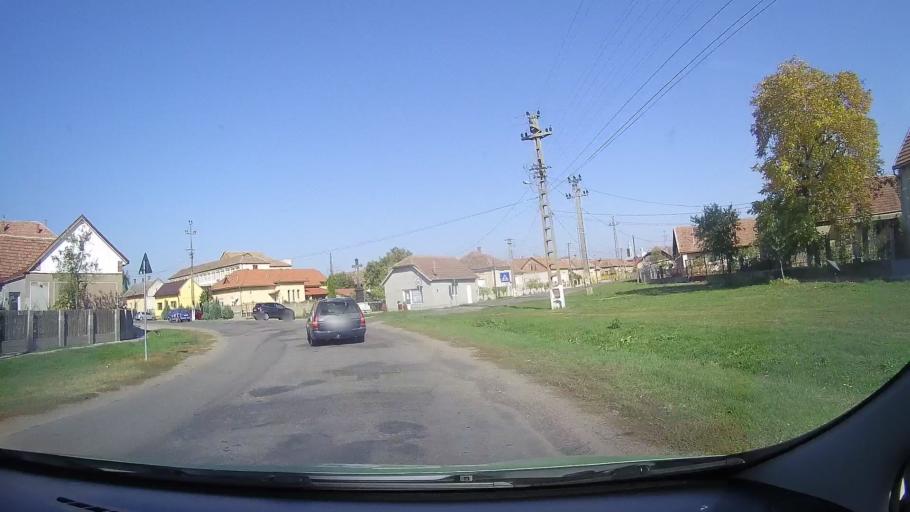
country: RO
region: Satu Mare
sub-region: Comuna Sanislau
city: Sanislau
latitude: 47.6364
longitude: 22.3261
